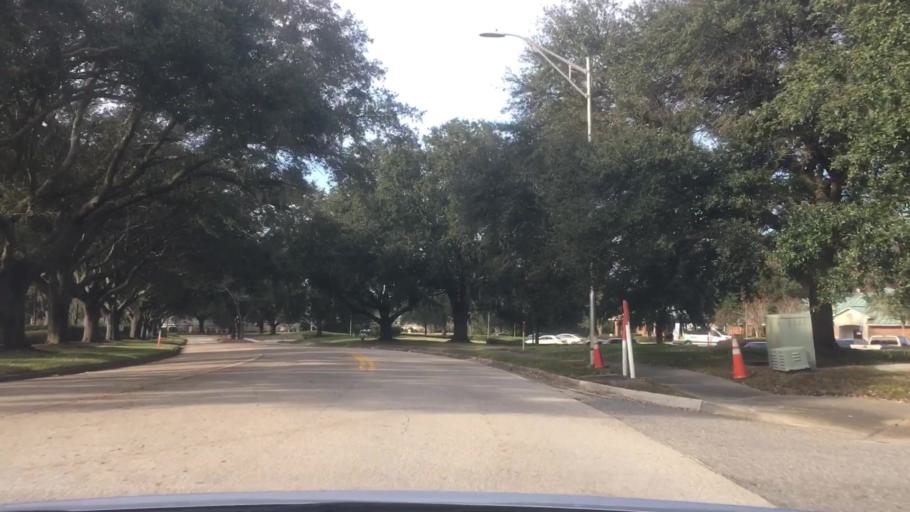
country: US
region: Florida
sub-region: Duval County
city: Jacksonville
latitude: 30.2568
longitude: -81.5861
